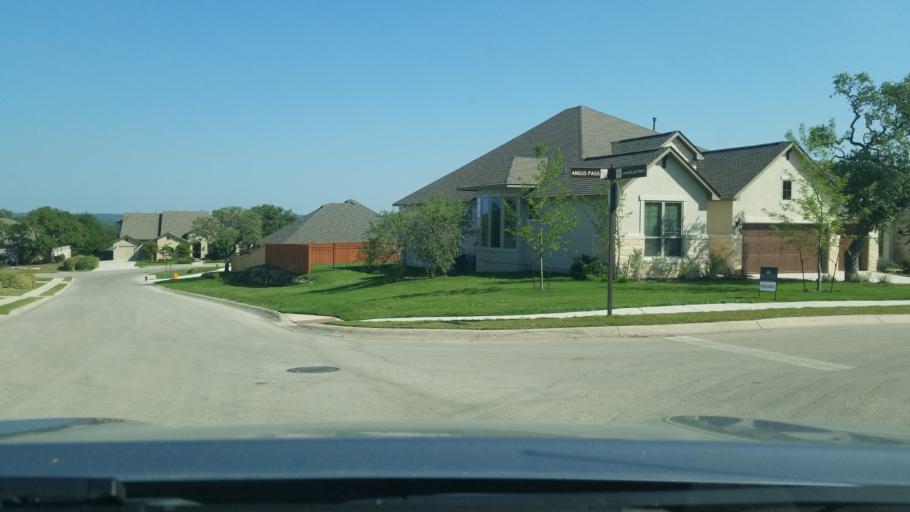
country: US
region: Texas
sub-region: Comal County
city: Bulverde
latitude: 29.7607
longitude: -98.4207
